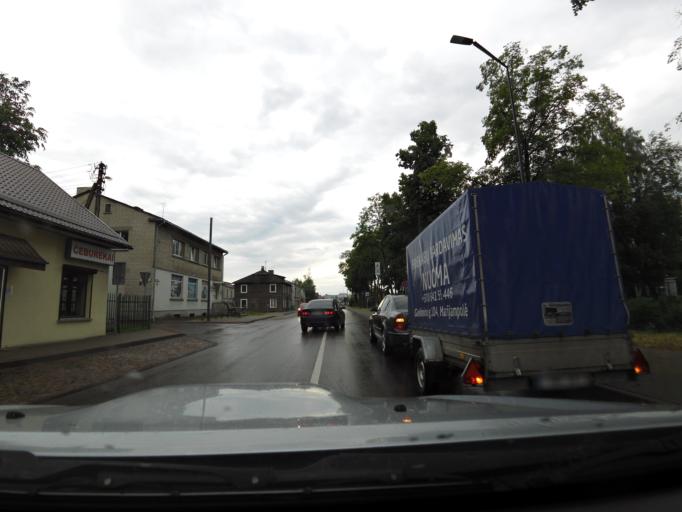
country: LT
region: Marijampoles apskritis
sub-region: Marijampole Municipality
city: Marijampole
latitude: 54.5557
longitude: 23.3593
